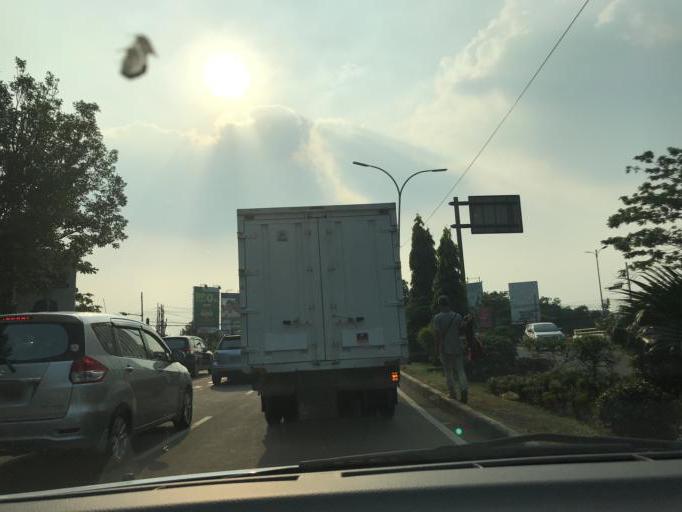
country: ID
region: West Java
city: Cibinong
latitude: -6.5188
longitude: 106.8366
